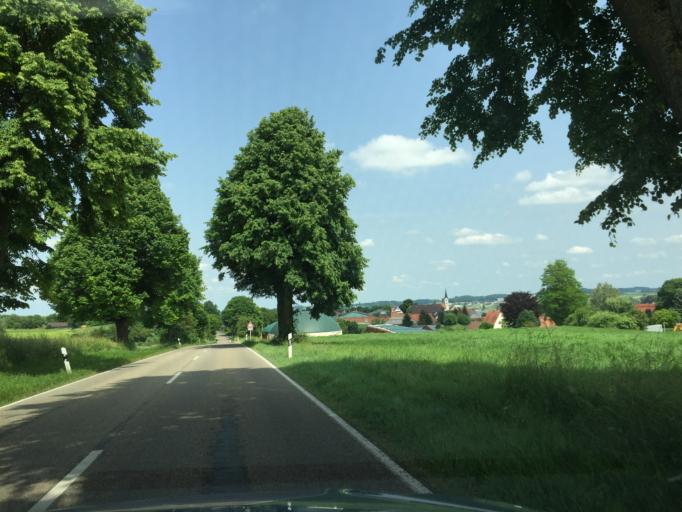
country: DE
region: Bavaria
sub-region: Swabia
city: Zusamaltheim
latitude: 48.5380
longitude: 10.6464
